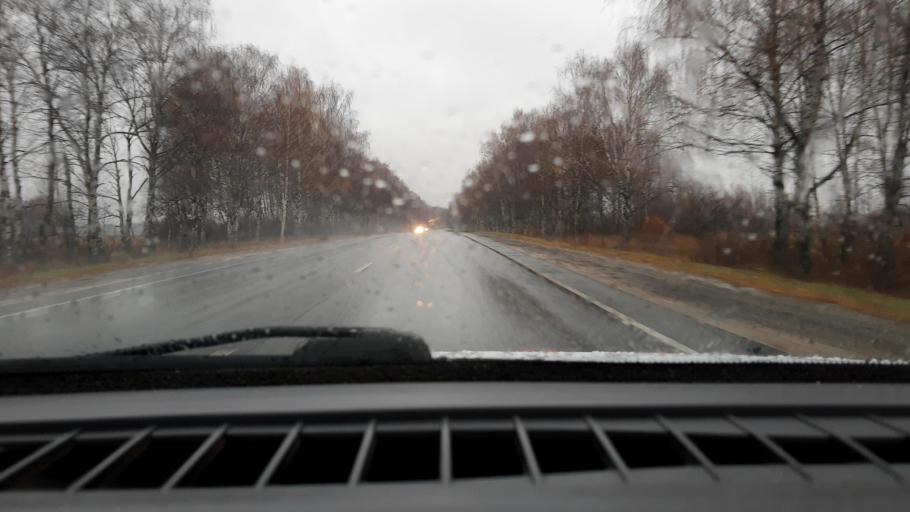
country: RU
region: Nizjnij Novgorod
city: Sitniki
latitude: 56.5320
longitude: 44.0235
